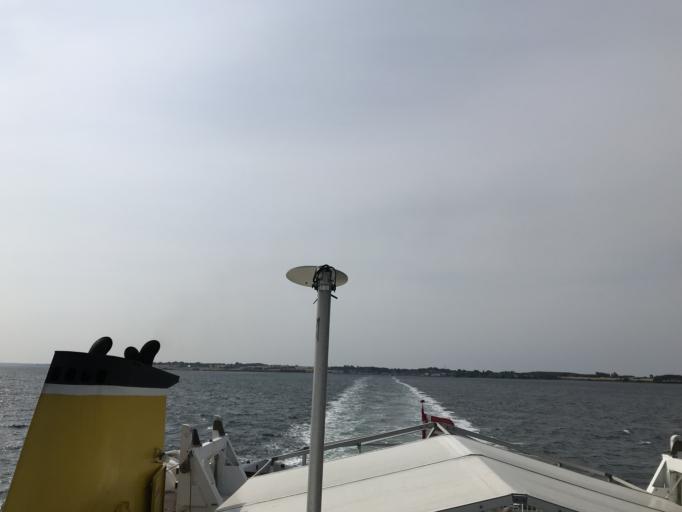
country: DK
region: South Denmark
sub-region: Faaborg-Midtfyn Kommune
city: Faaborg
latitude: 54.9629
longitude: 10.2529
